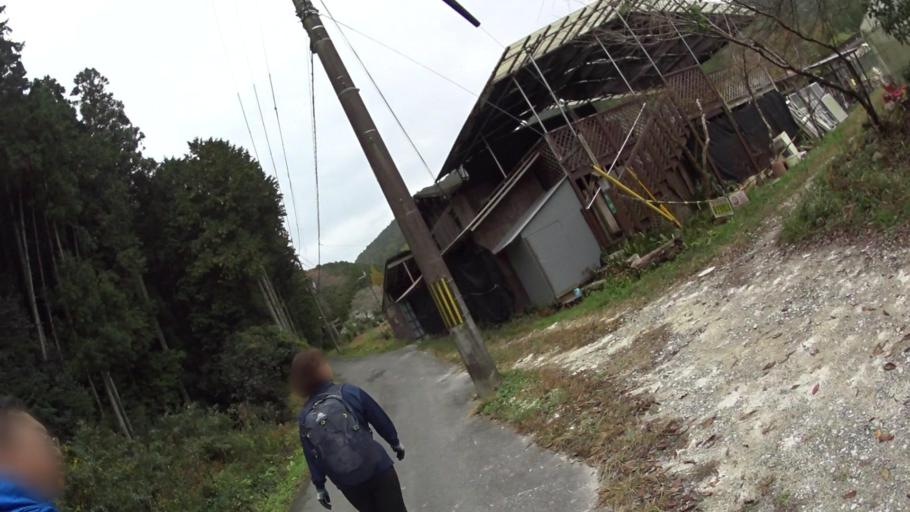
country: JP
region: Kyoto
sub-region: Kyoto-shi
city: Kamigyo-ku
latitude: 35.1094
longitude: 135.8182
